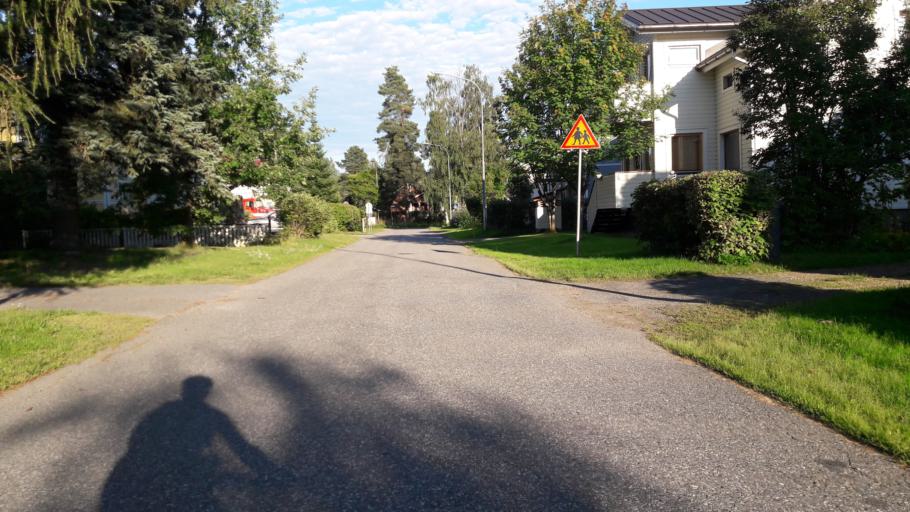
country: FI
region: North Karelia
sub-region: Joensuu
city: Joensuu
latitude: 62.6101
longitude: 29.7534
